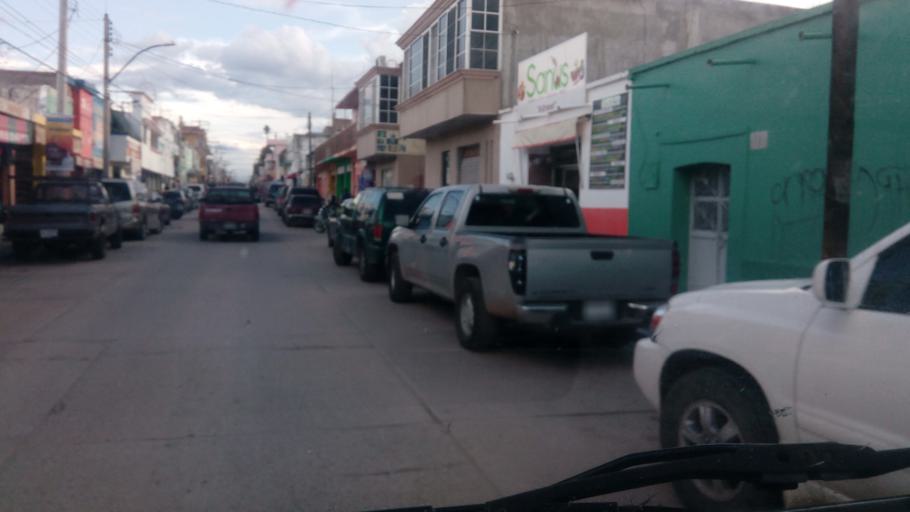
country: MX
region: Durango
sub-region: Santiago Papasquiaro
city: Santiago Papasquiaro
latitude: 25.0466
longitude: -105.4206
